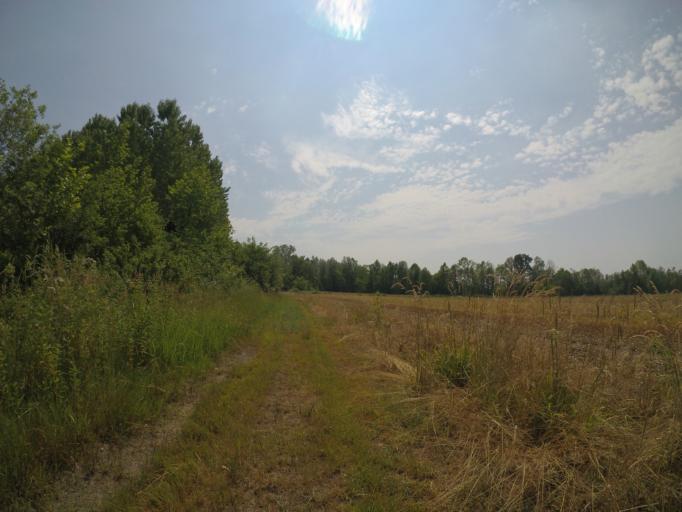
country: IT
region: Friuli Venezia Giulia
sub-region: Provincia di Udine
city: Bertiolo
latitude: 45.9182
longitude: 13.0349
